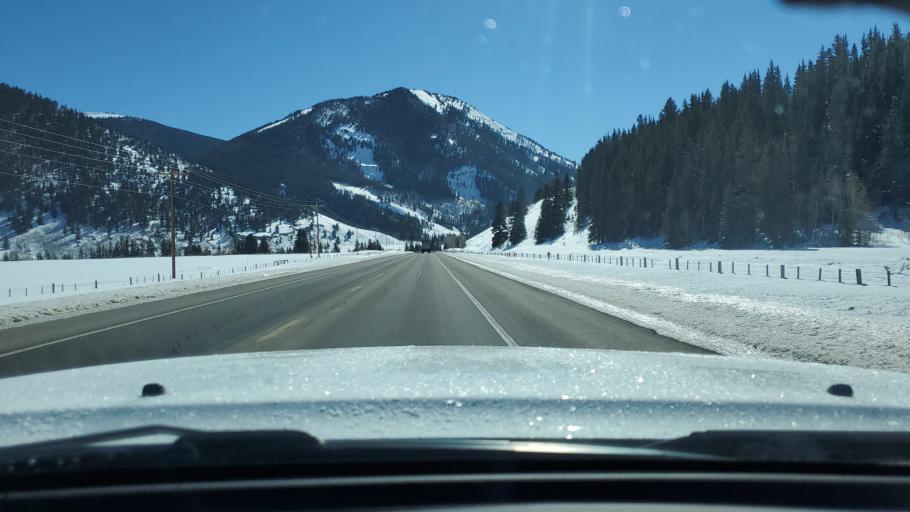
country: US
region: Colorado
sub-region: Gunnison County
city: Crested Butte
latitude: 38.7996
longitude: -106.8832
